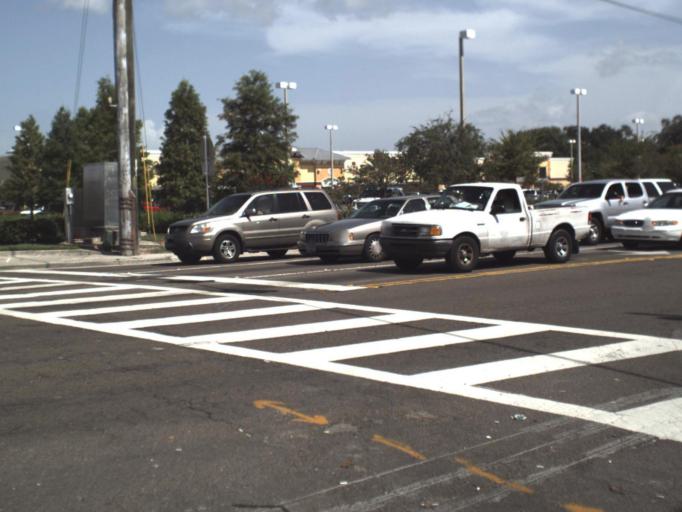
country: US
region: Florida
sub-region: Pinellas County
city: Clearwater
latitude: 27.9604
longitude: -82.7463
